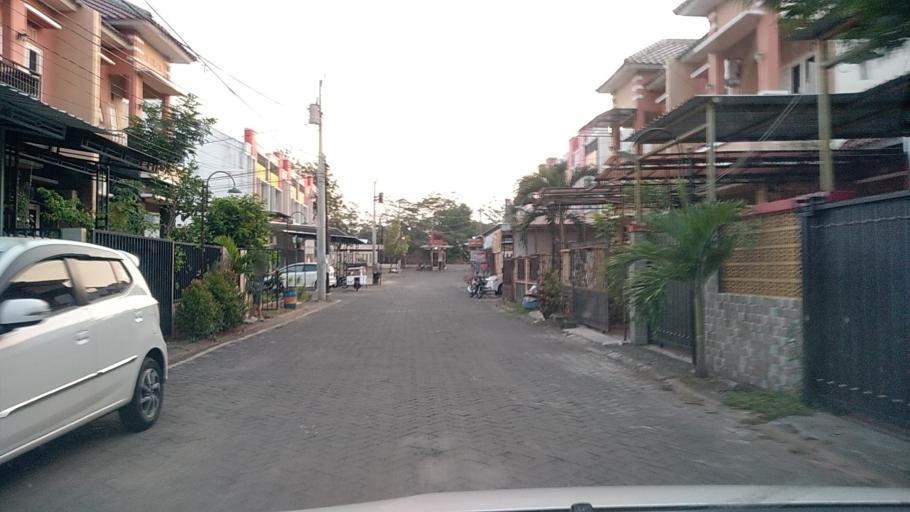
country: ID
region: Central Java
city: Ungaran
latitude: -7.0715
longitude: 110.4428
